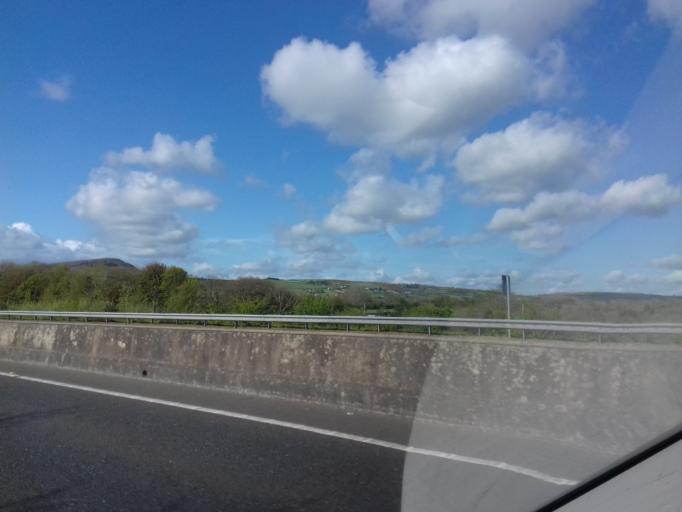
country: IE
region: Munster
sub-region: Waterford
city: Waterford
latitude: 52.3155
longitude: -7.1417
